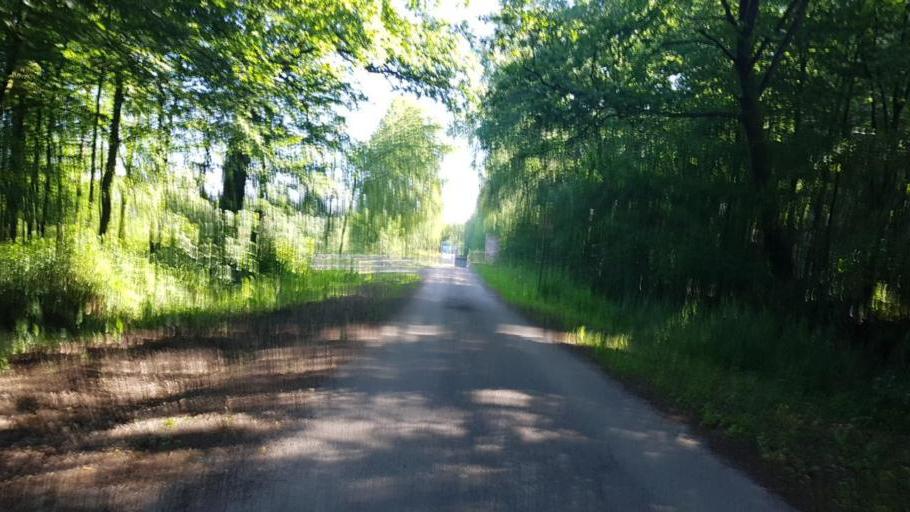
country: FR
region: Picardie
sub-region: Departement de l'Aisne
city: Hirson
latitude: 49.9404
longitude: 4.0955
